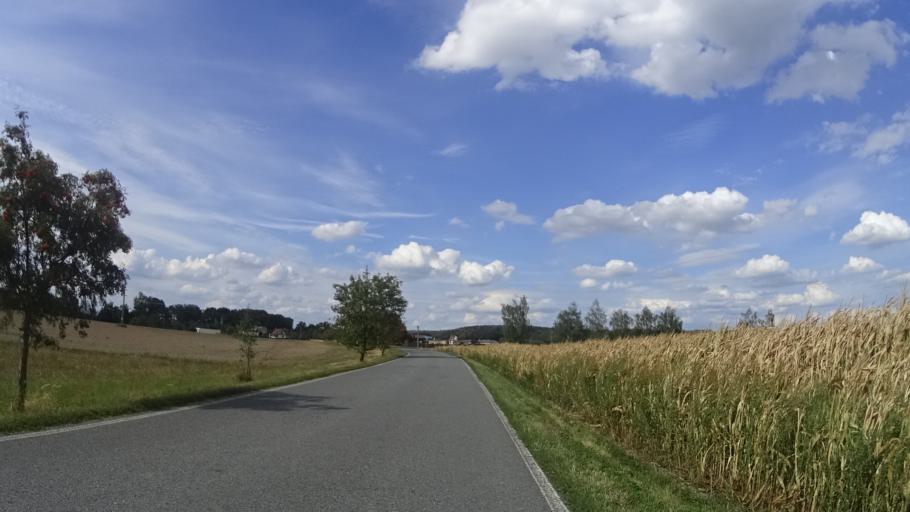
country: CZ
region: Olomoucky
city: Moravicany
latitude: 49.7394
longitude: 16.9740
